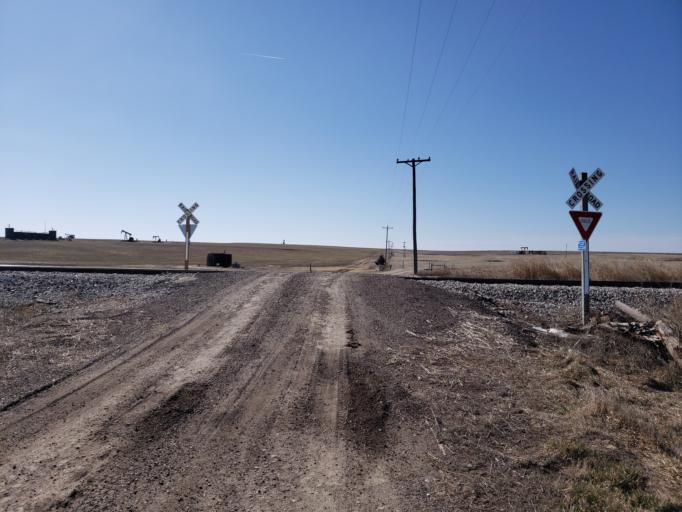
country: US
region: Kansas
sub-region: Ness County
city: Ness City
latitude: 38.4508
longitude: -99.9723
